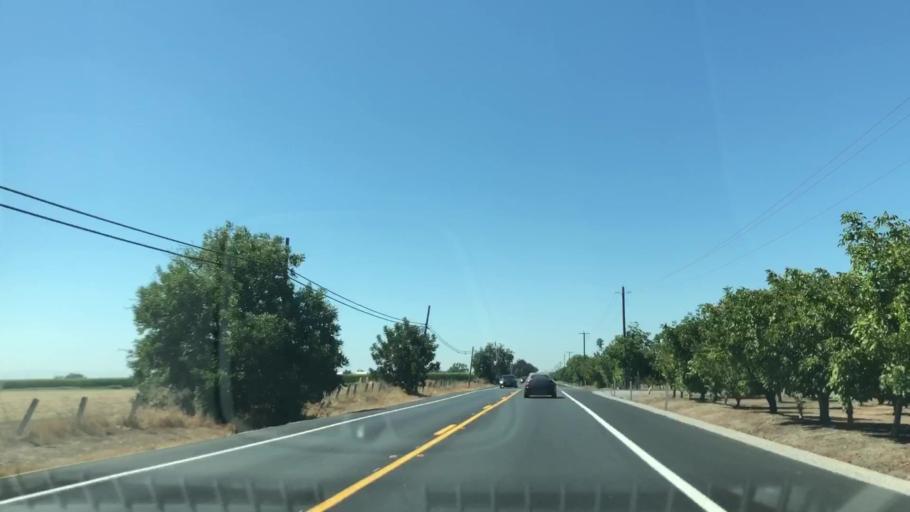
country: US
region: California
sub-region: San Joaquin County
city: Garden Acres
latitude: 37.9494
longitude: -121.2011
